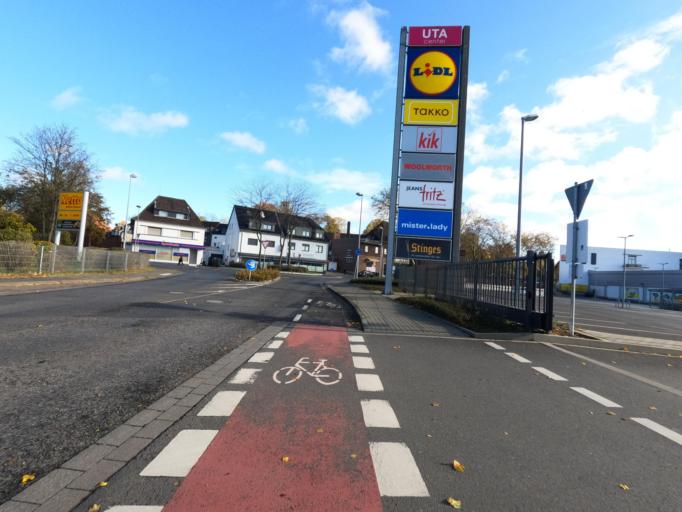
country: DE
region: North Rhine-Westphalia
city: Huckelhoven
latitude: 51.0569
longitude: 6.2195
